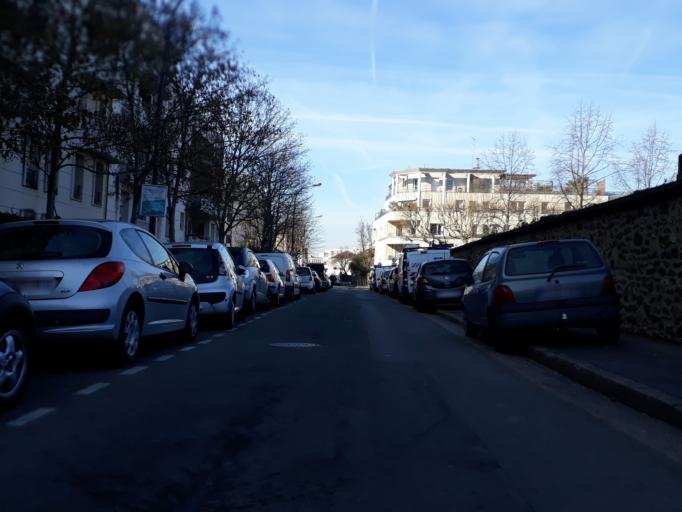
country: FR
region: Ile-de-France
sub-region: Departement des Hauts-de-Seine
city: Asnieres-sur-Seine
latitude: 48.9179
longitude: 2.2876
